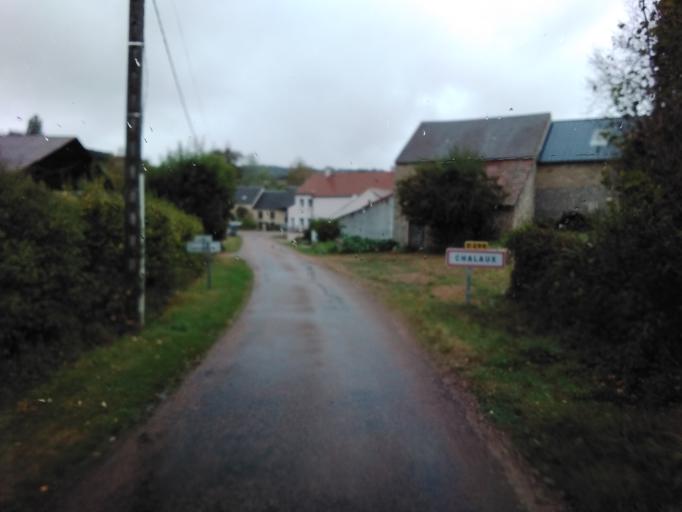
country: FR
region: Bourgogne
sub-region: Departement de la Nievre
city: Lormes
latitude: 47.3411
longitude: 3.9162
